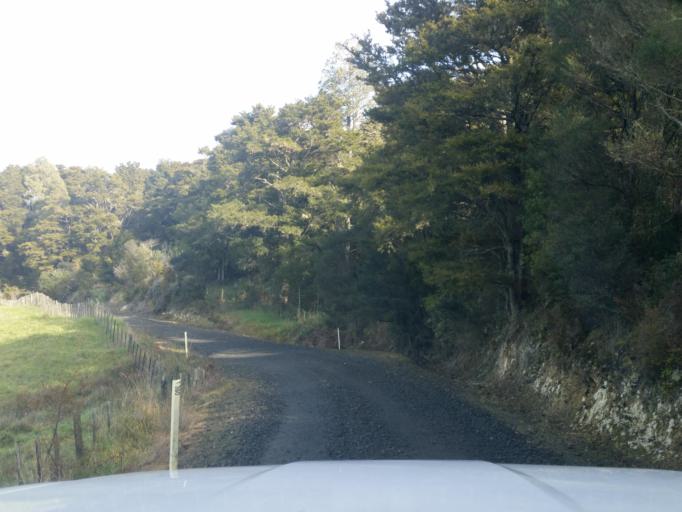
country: NZ
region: Northland
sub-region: Kaipara District
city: Dargaville
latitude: -35.8289
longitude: 173.9011
